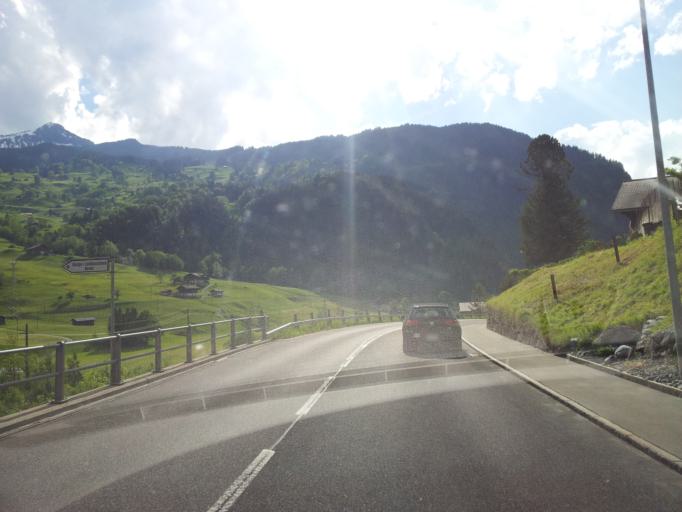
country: CH
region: Bern
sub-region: Interlaken-Oberhasli District
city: Grindelwald
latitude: 46.6262
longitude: 8.0156
